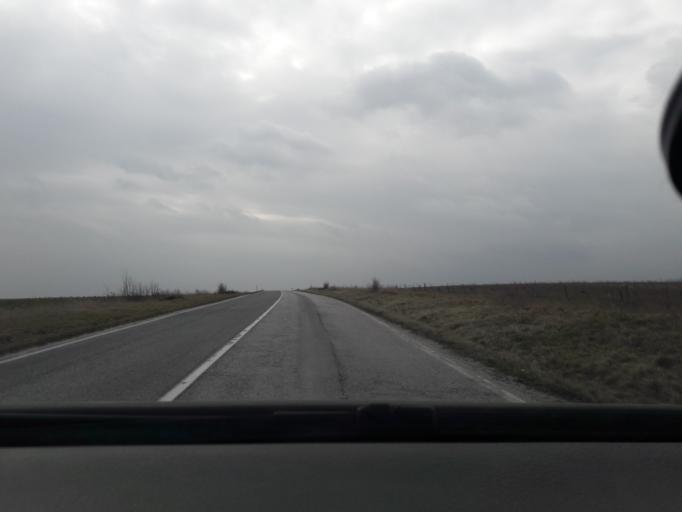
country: SK
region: Trnavsky
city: Smolenice
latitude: 48.4351
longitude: 17.4242
